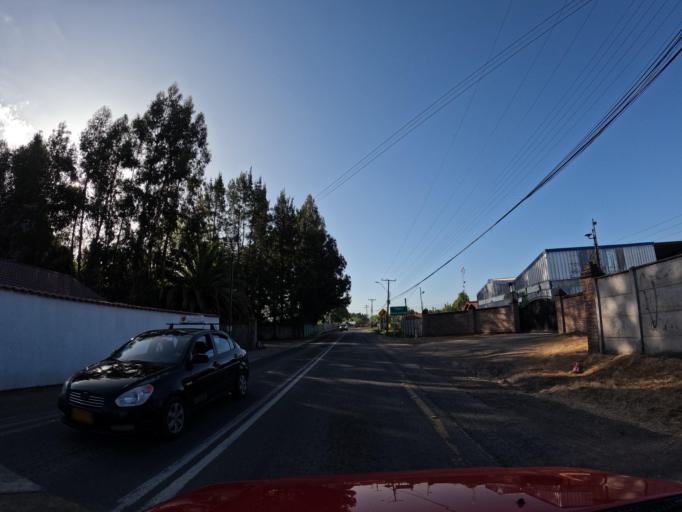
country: CL
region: O'Higgins
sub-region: Provincia de Colchagua
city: Santa Cruz
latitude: -34.6571
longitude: -71.3423
